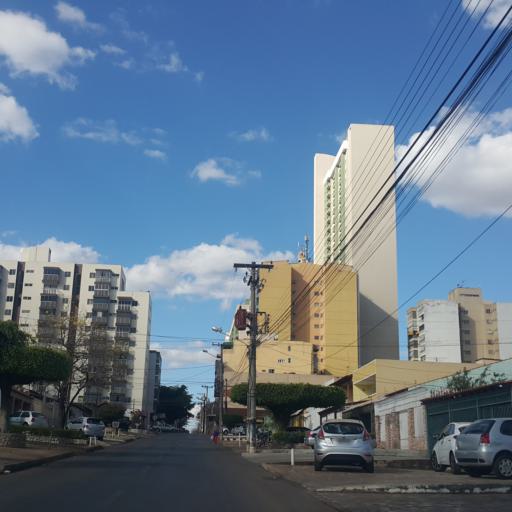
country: BR
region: Federal District
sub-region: Brasilia
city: Brasilia
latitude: -15.8272
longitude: -48.0619
